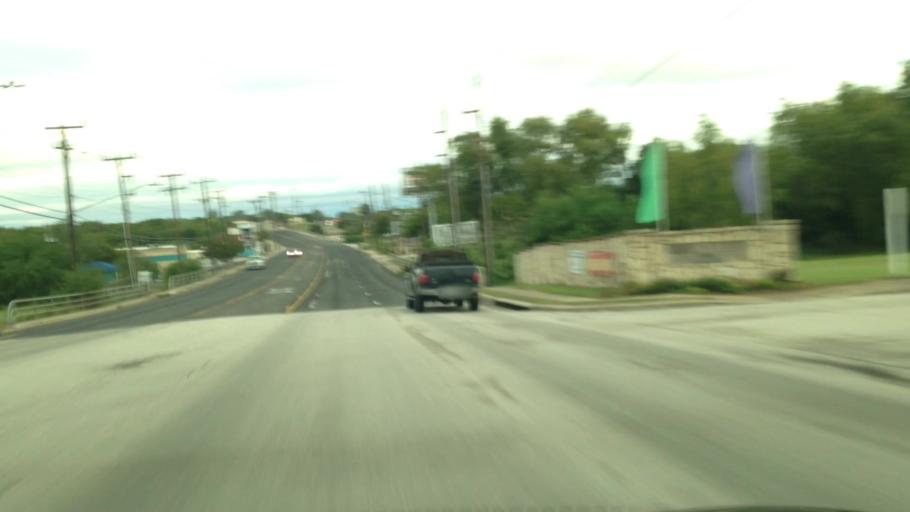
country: US
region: Texas
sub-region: Bexar County
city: Live Oak
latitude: 29.5638
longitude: -98.3630
